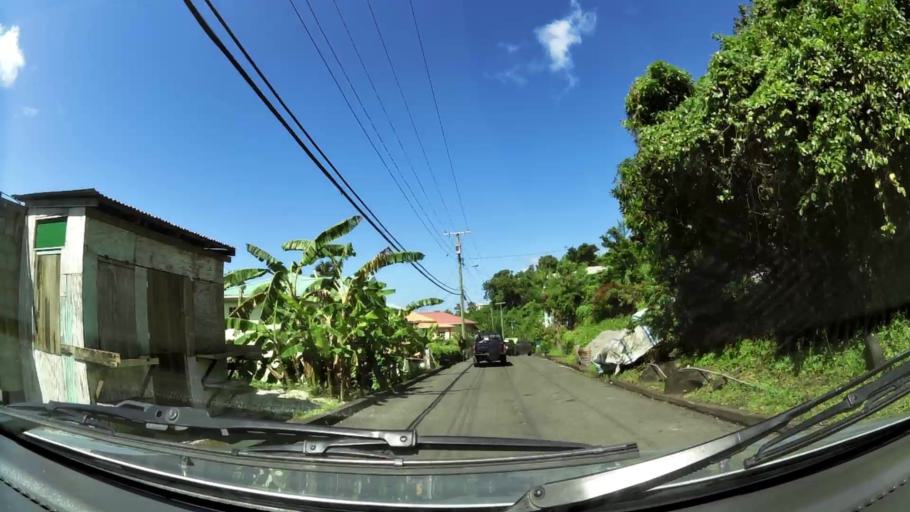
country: GD
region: Saint John
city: Gouyave
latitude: 12.1275
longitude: -61.7472
